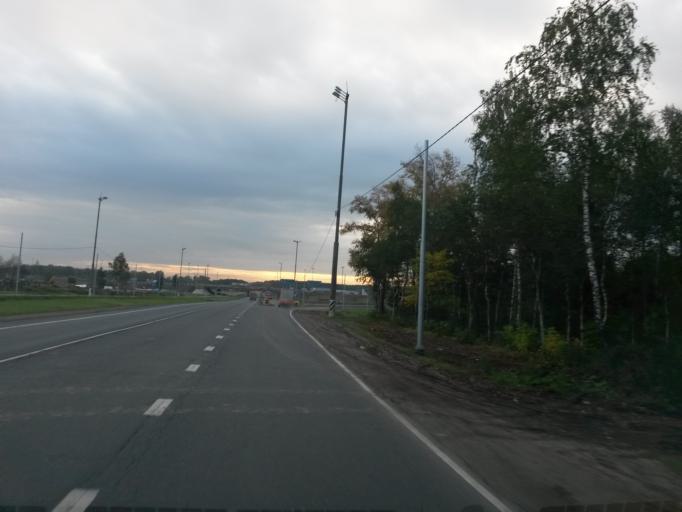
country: RU
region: Moskovskaya
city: L'vovskiy
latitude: 55.3320
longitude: 37.5587
